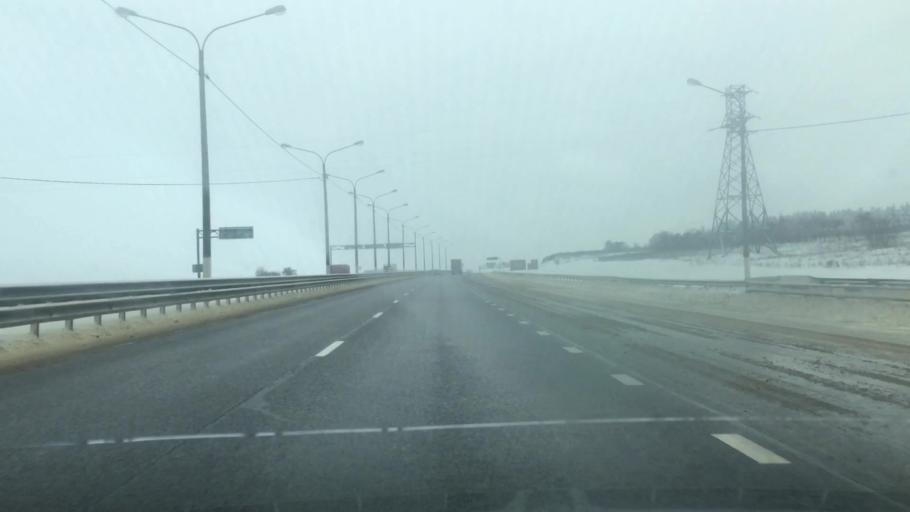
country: RU
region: Tula
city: Yefremov
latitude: 53.1606
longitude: 38.2492
